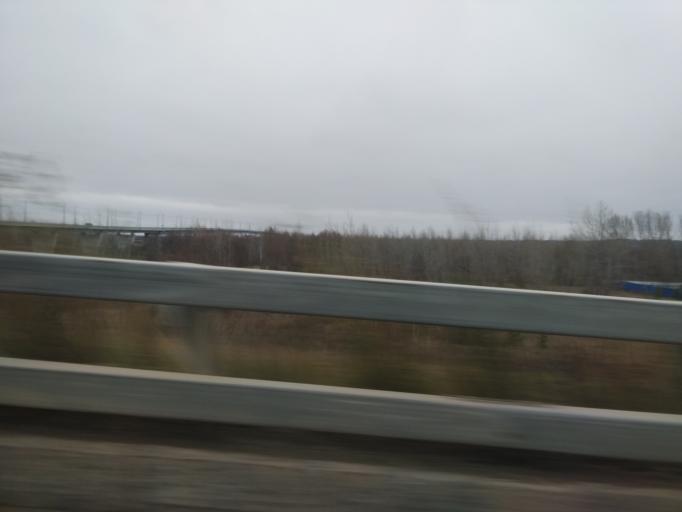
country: RU
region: Kirov
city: Sosnovka
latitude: 56.2498
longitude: 51.2177
